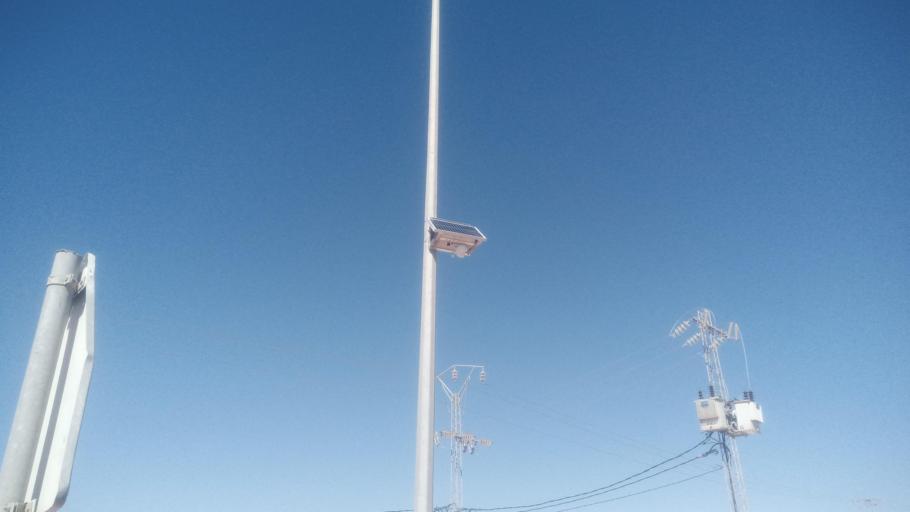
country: TN
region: Tawzar
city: Degache
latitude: 33.9582
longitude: 8.1873
